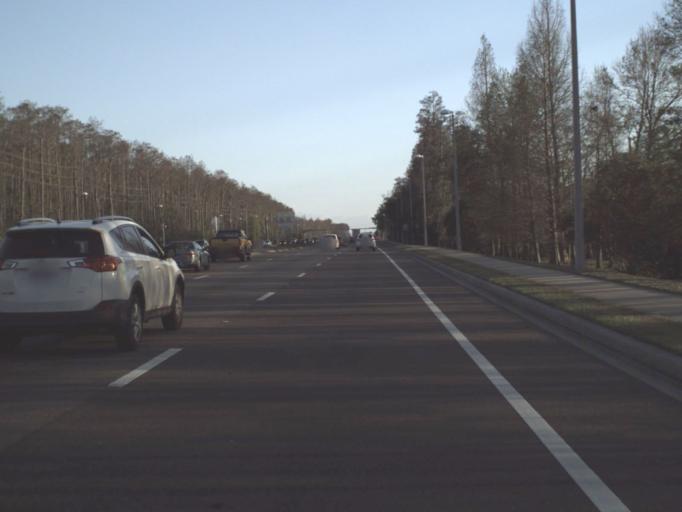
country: US
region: Florida
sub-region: Orange County
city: Hunters Creek
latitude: 28.3671
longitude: -81.4046
